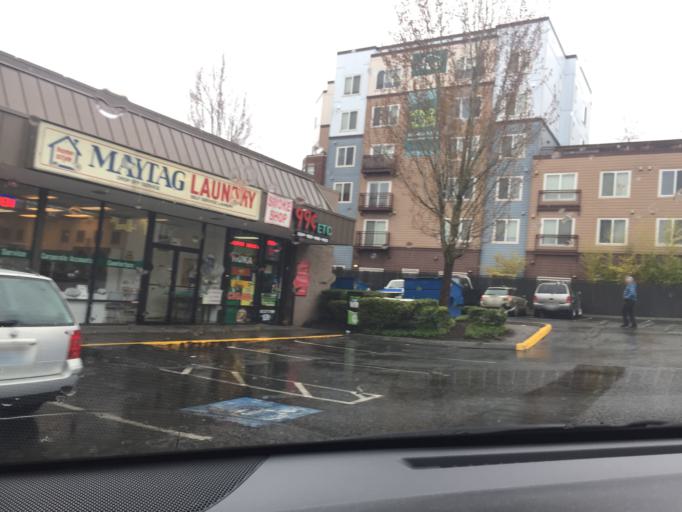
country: US
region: Washington
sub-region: King County
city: Lake Forest Park
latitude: 47.7215
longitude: -122.2958
